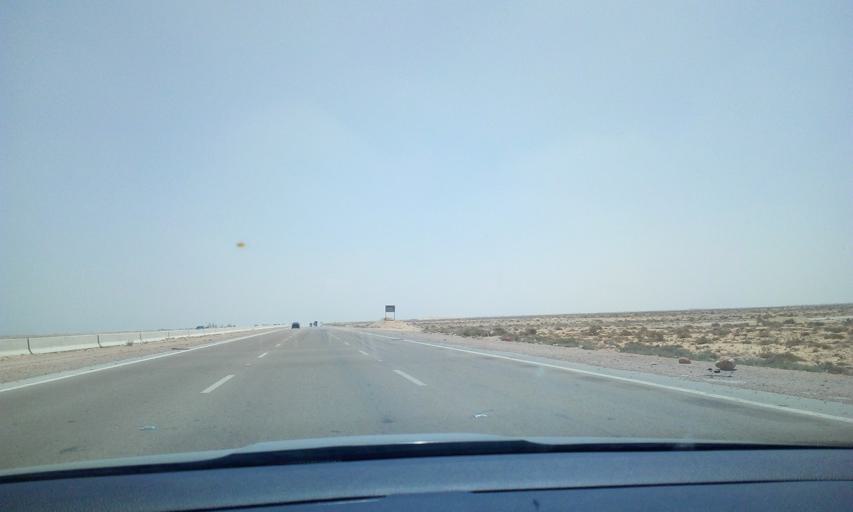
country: EG
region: Al Buhayrah
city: Abu al Matamir
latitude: 30.5985
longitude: 29.8574
